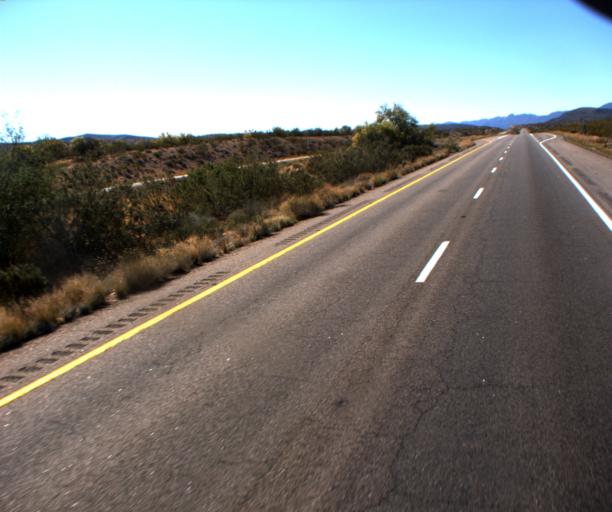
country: US
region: Arizona
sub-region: Yavapai County
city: Bagdad
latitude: 34.6118
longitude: -113.5258
